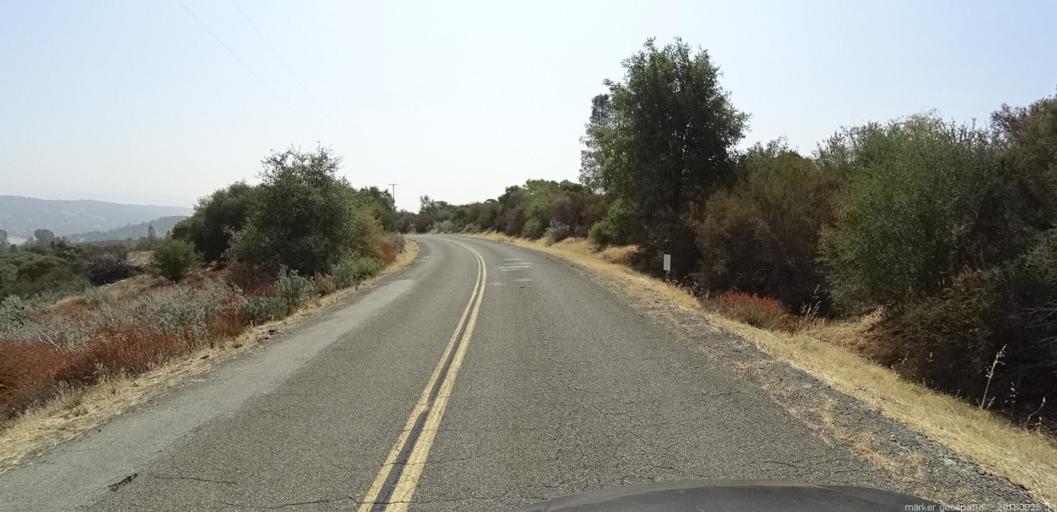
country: US
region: California
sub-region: San Luis Obispo County
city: San Miguel
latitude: 35.9208
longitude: -120.5229
